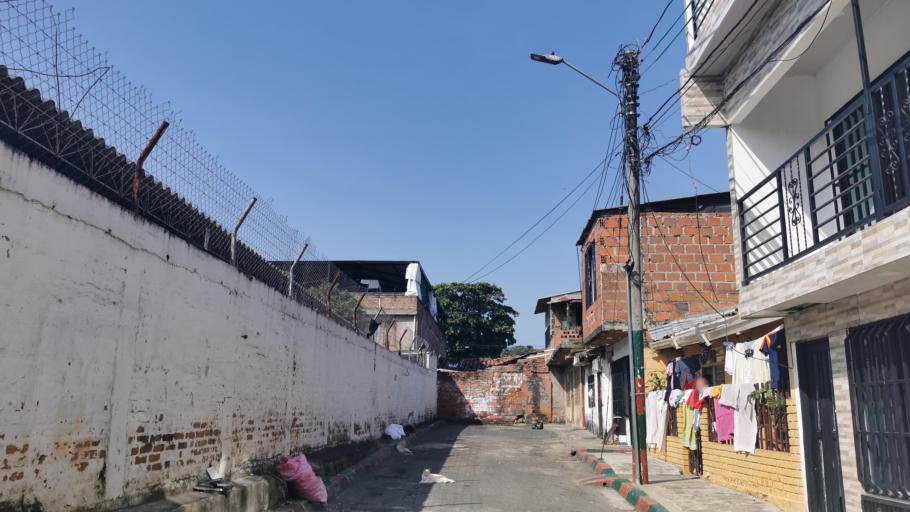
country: CO
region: Valle del Cauca
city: Jamundi
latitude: 3.2637
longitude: -76.5447
